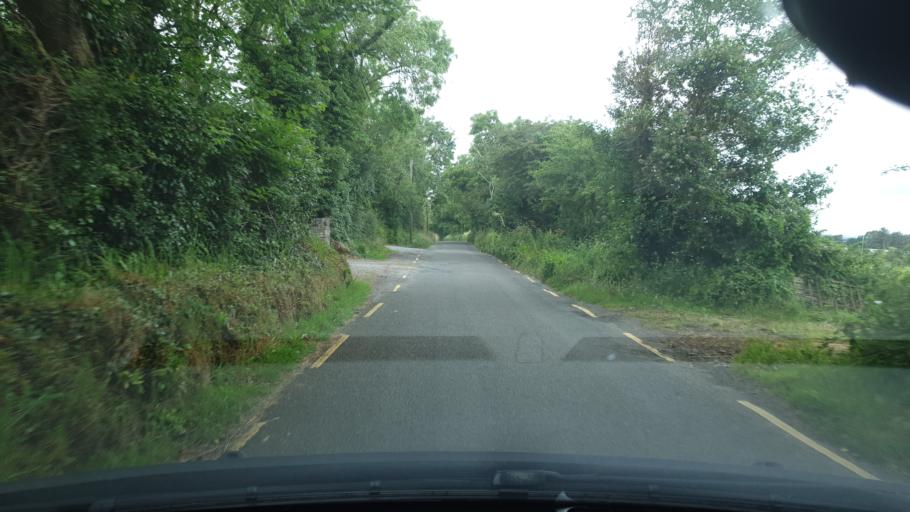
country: IE
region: Munster
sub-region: Ciarrai
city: Tralee
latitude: 52.2424
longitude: -9.6520
